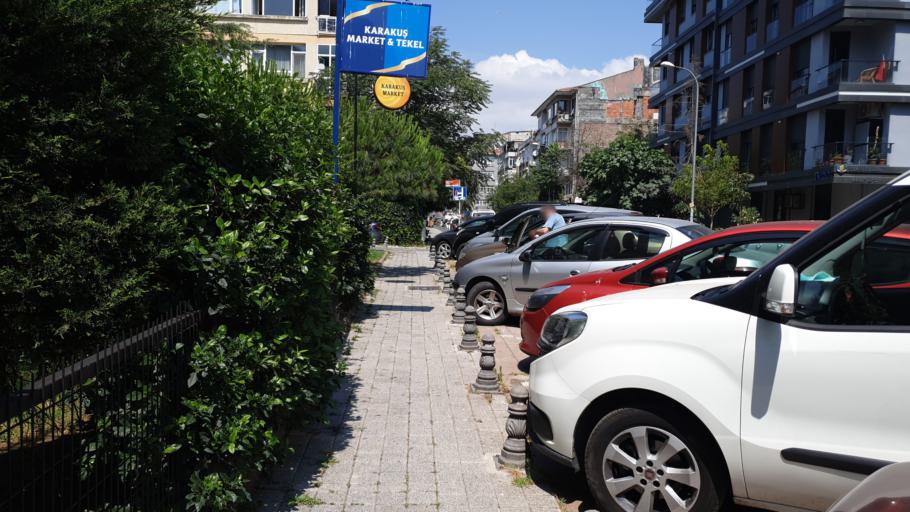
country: TR
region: Istanbul
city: UEskuedar
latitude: 40.9876
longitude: 29.0334
